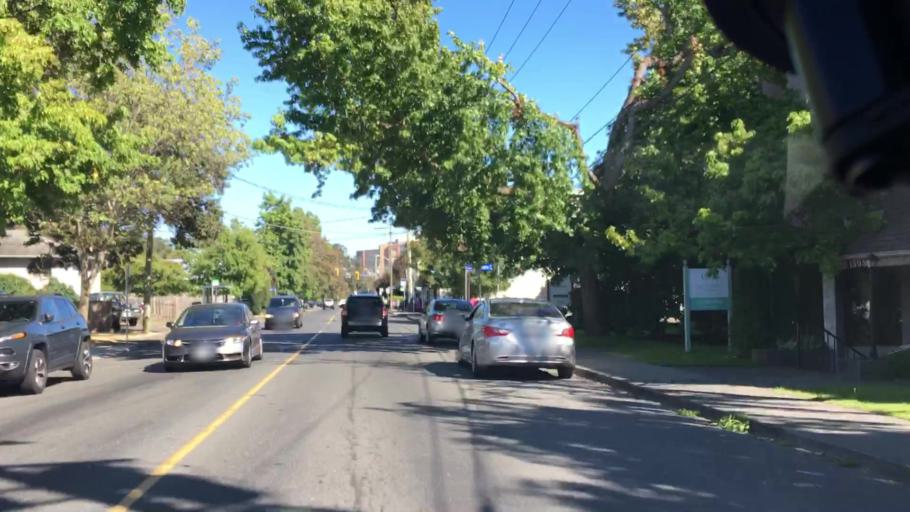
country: CA
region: British Columbia
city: Victoria
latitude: 48.4340
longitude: -123.3362
